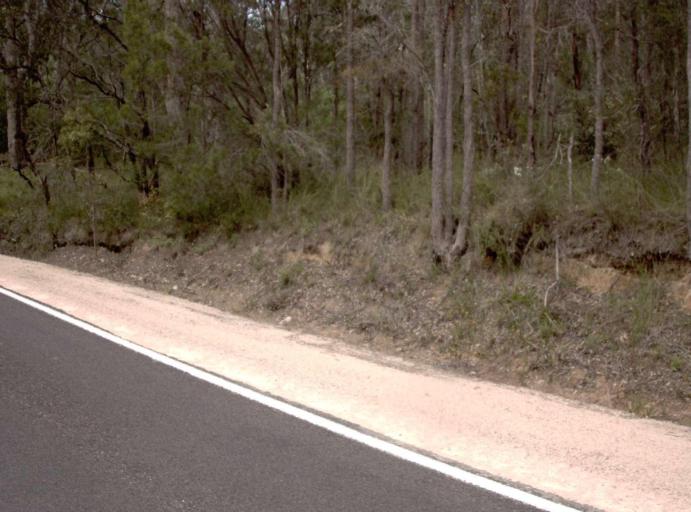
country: AU
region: New South Wales
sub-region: Bega Valley
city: Eden
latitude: -37.4391
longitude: 149.6445
